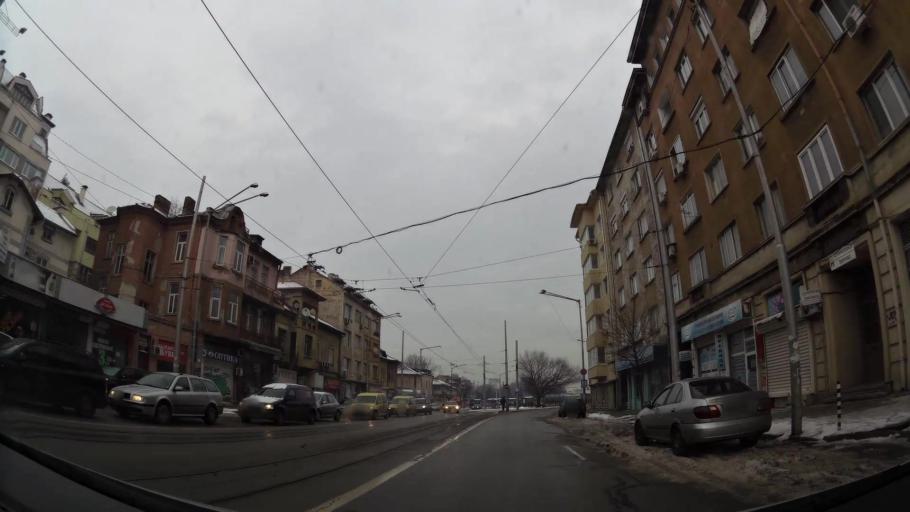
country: BG
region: Sofia-Capital
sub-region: Stolichna Obshtina
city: Sofia
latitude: 42.7096
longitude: 23.3184
